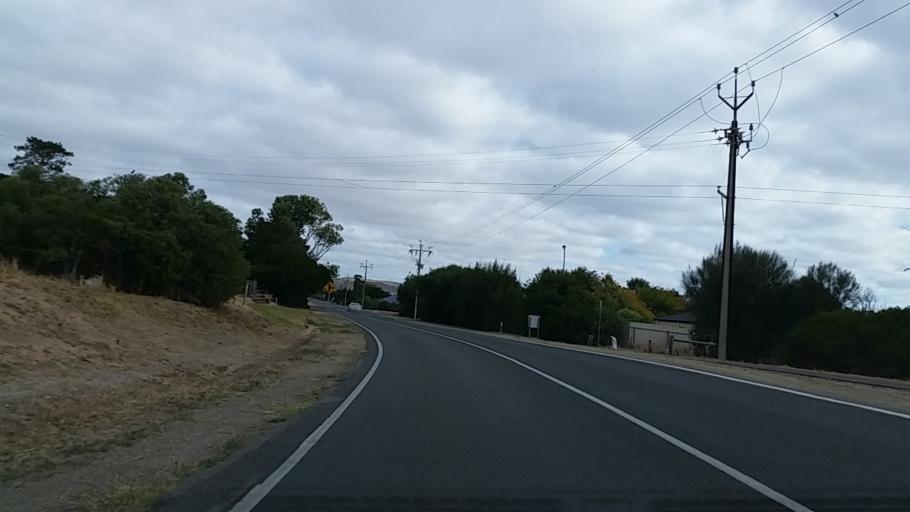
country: AU
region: South Australia
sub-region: Yankalilla
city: Normanville
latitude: -35.4342
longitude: 138.3217
